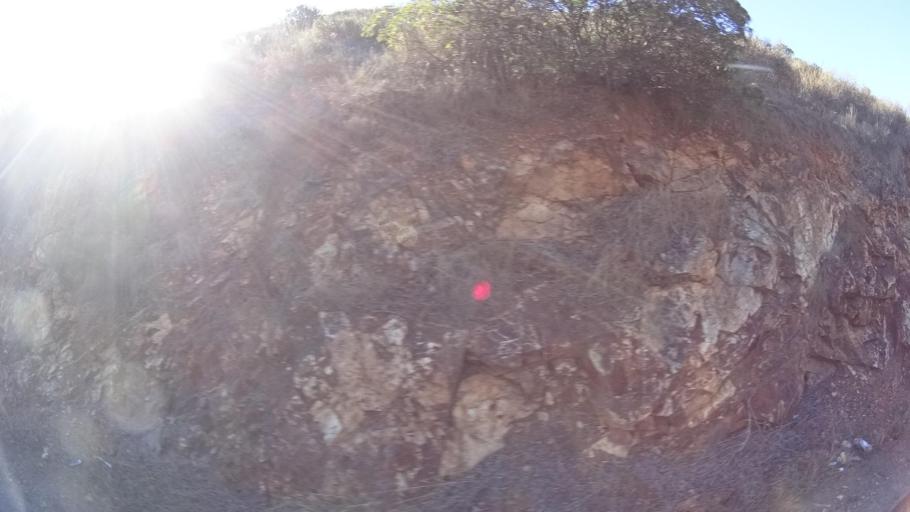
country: US
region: California
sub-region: San Diego County
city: Jamul
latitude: 32.6401
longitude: -116.8806
